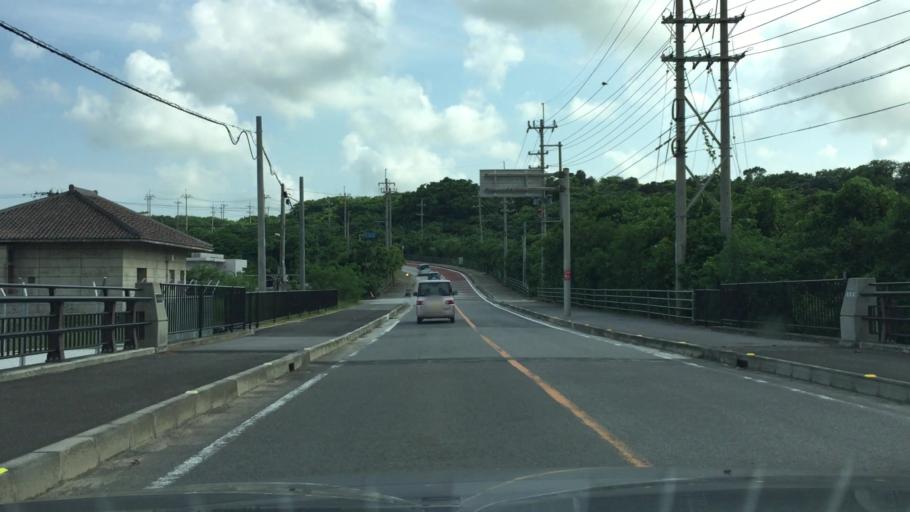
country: JP
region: Okinawa
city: Ishigaki
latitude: 24.4328
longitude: 124.2480
